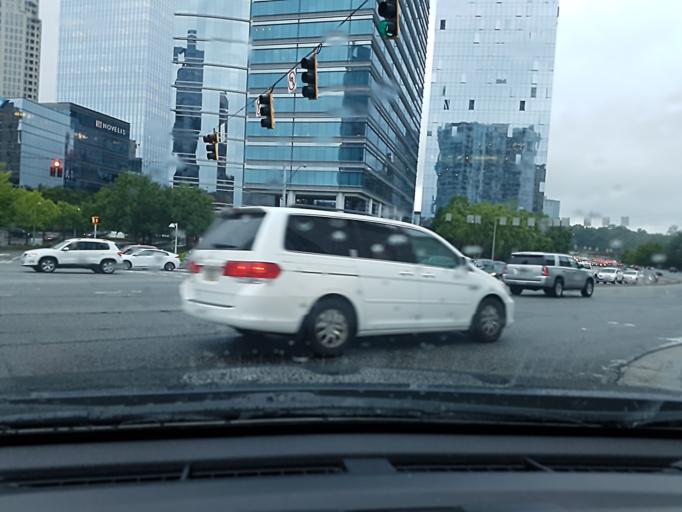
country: US
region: Georgia
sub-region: DeKalb County
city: North Atlanta
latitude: 33.8529
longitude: -84.3654
